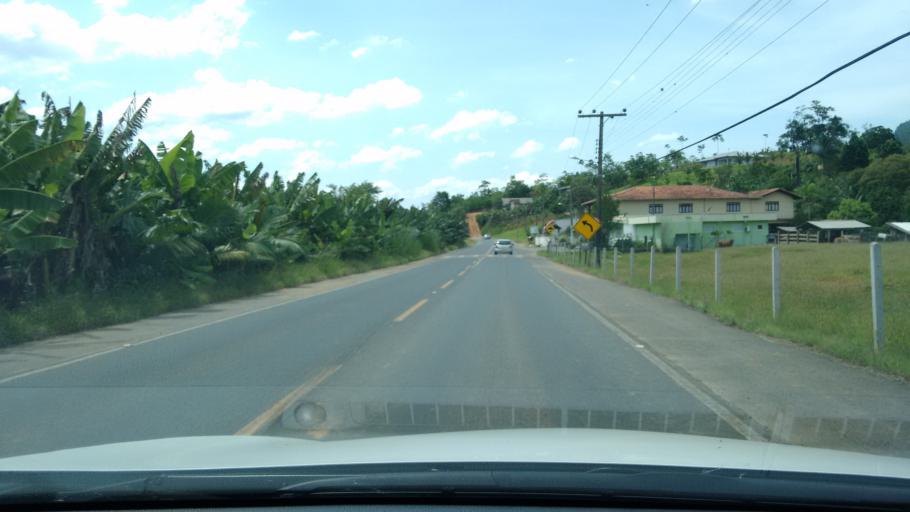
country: BR
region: Santa Catarina
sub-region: Rodeio
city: Gavea
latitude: -26.8610
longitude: -49.3340
